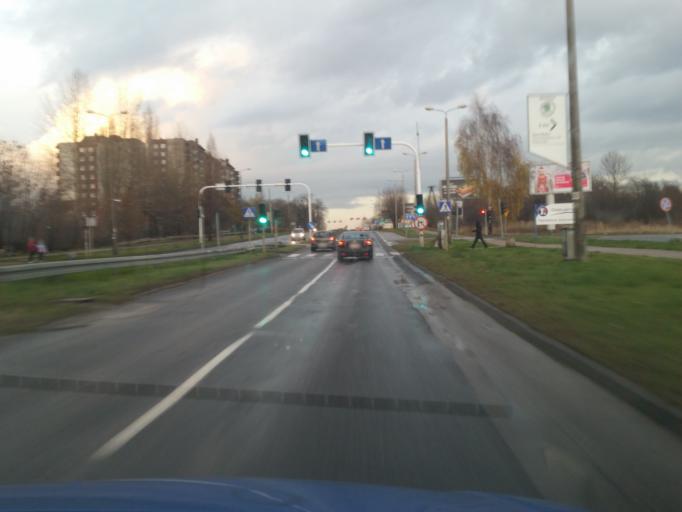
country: PL
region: Silesian Voivodeship
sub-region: Dabrowa Gornicza
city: Dabrowa Gornicza
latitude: 50.2931
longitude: 19.1825
